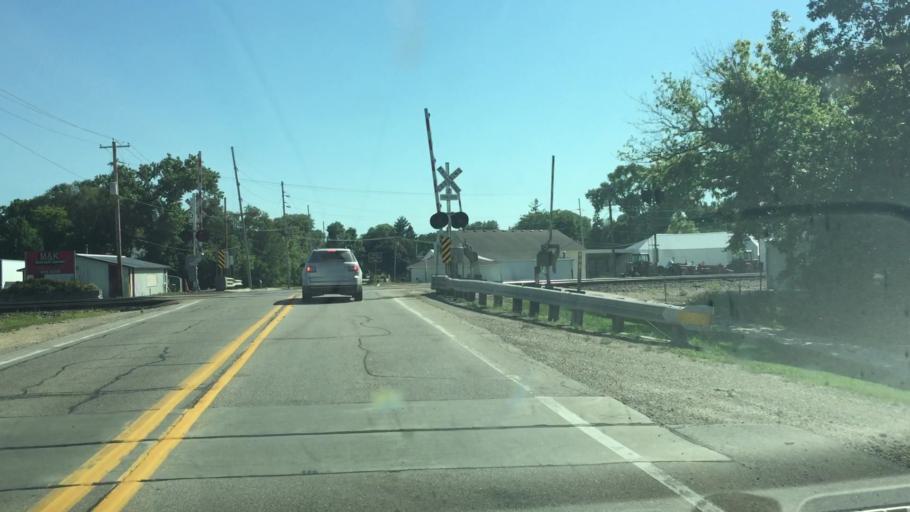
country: US
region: Iowa
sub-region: Linn County
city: Mount Vernon
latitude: 41.9300
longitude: -91.4096
